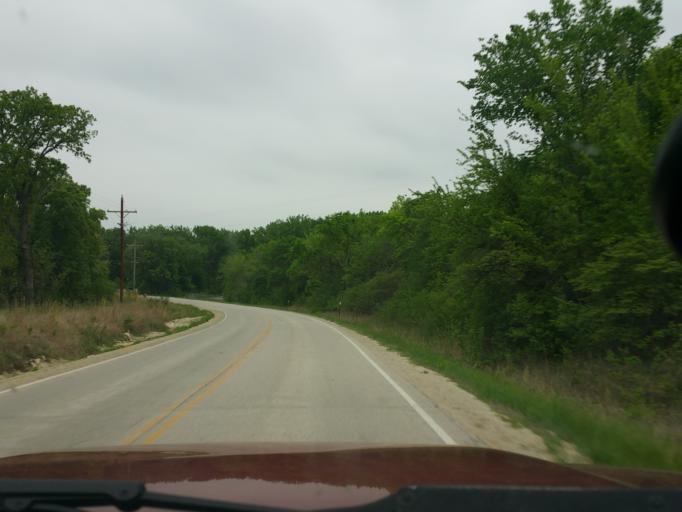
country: US
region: Kansas
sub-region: Riley County
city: Manhattan
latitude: 39.2539
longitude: -96.5710
